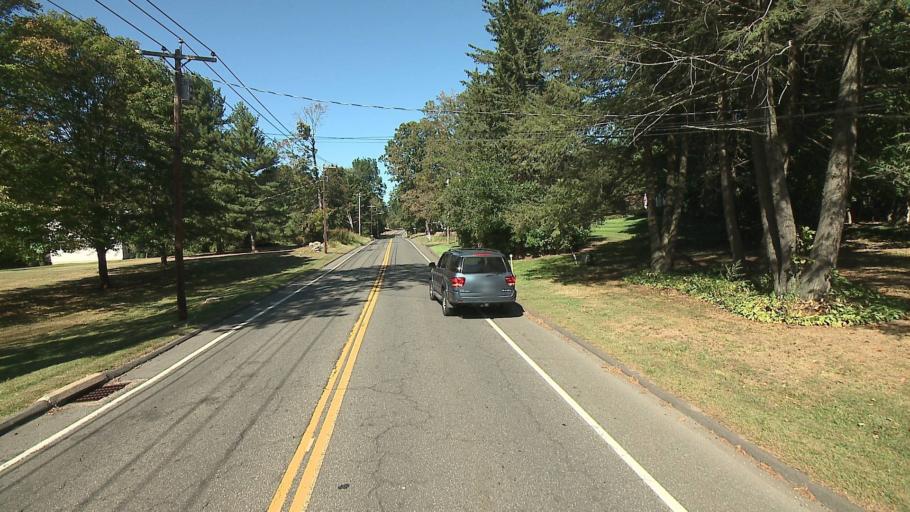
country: US
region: Connecticut
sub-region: New Haven County
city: Woodbridge
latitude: 41.3317
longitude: -73.0256
